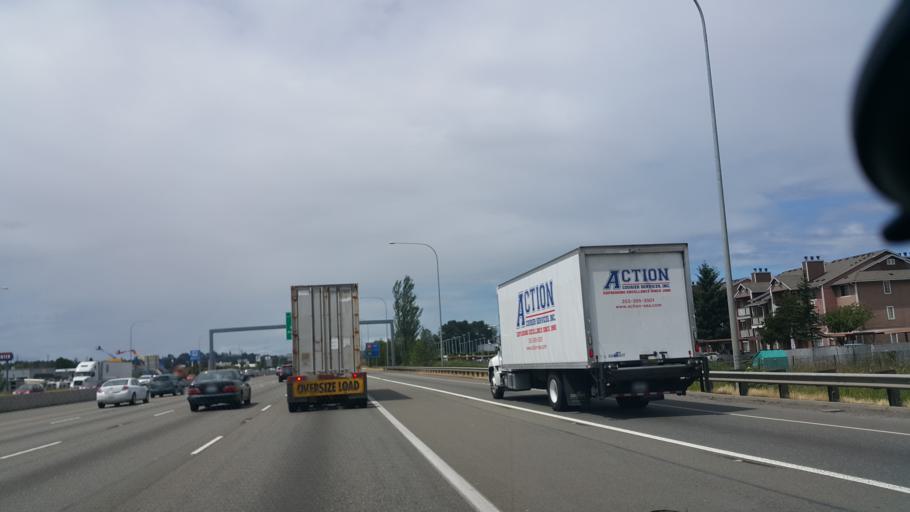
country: US
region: Washington
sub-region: Pierce County
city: Fife
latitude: 47.2426
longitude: -122.3665
